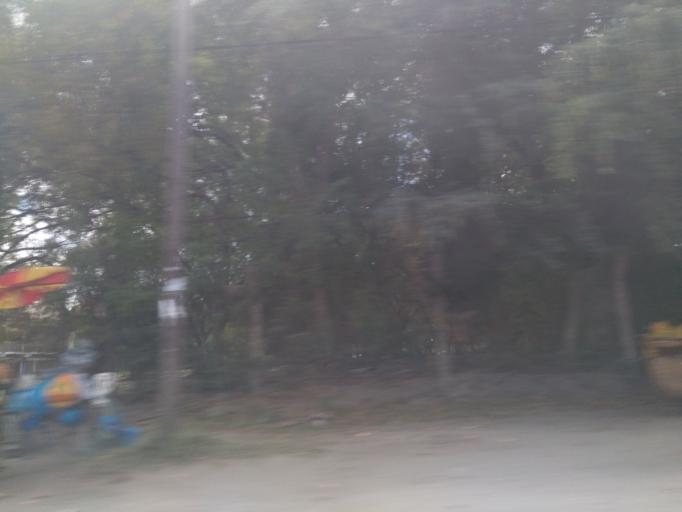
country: TZ
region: Dar es Salaam
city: Dar es Salaam
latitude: -6.8482
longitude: 39.2744
